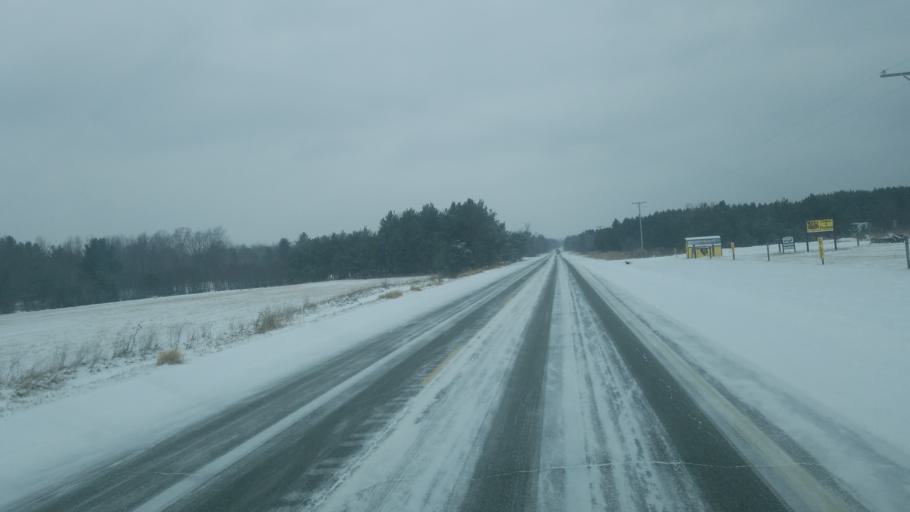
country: US
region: Michigan
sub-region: Osceola County
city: Evart
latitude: 43.9320
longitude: -85.1484
